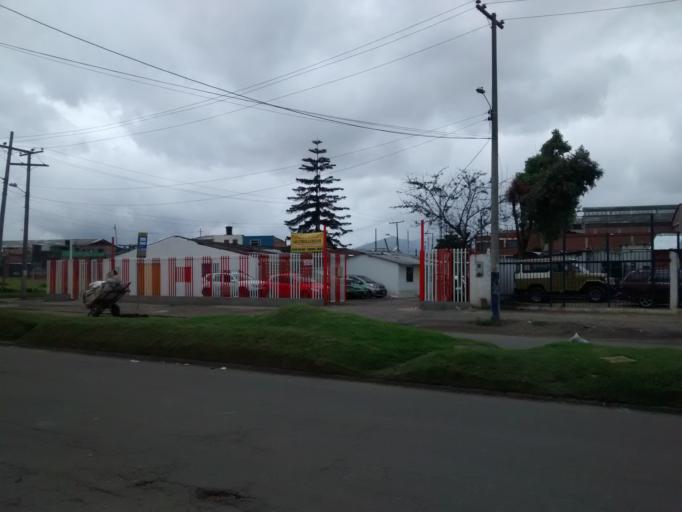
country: CO
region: Bogota D.C.
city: Bogota
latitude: 4.6936
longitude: -74.1193
